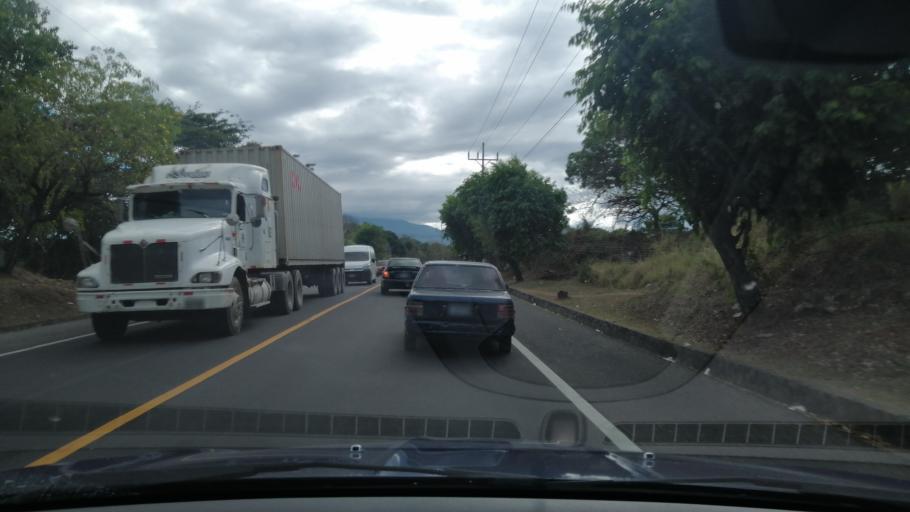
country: SV
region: Santa Ana
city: Santa Ana
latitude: 13.9875
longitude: -89.5447
